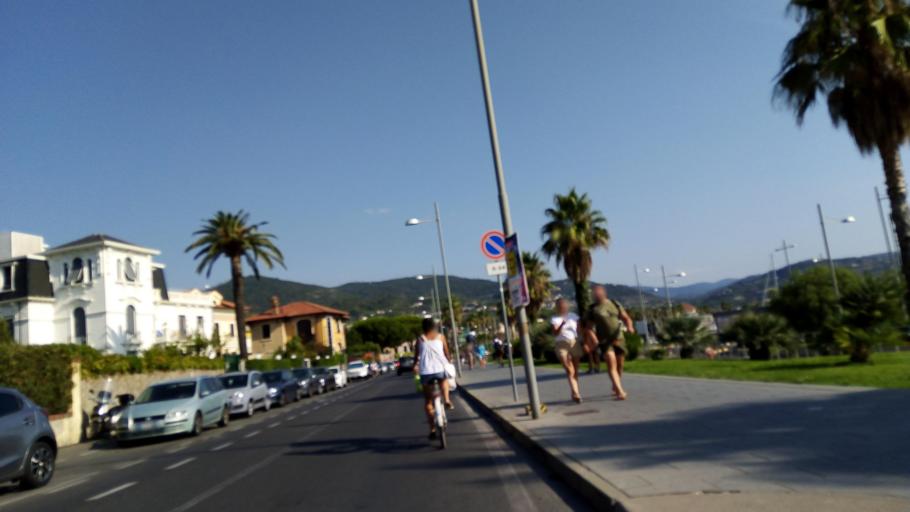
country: IT
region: Liguria
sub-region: Provincia di Savona
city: Loano
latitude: 44.1308
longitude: 8.2630
